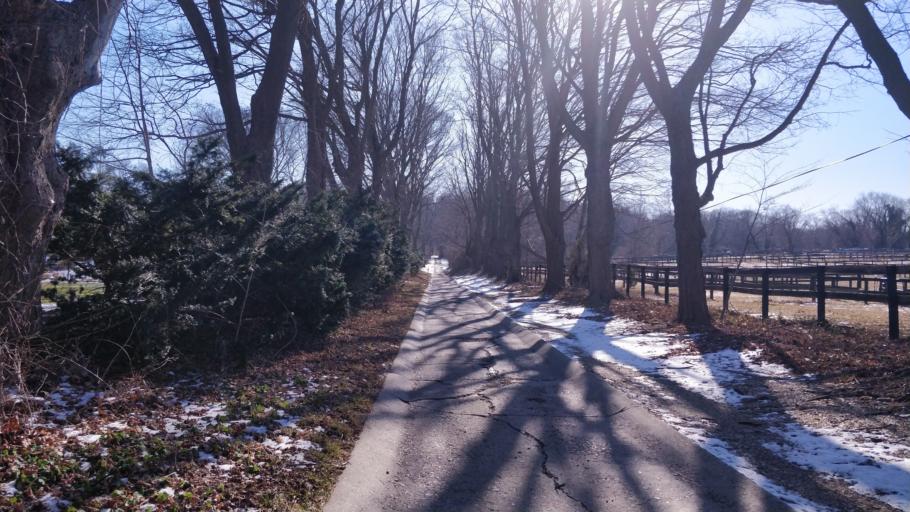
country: US
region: New York
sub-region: Nassau County
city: Brookville
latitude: 40.8118
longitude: -73.5846
